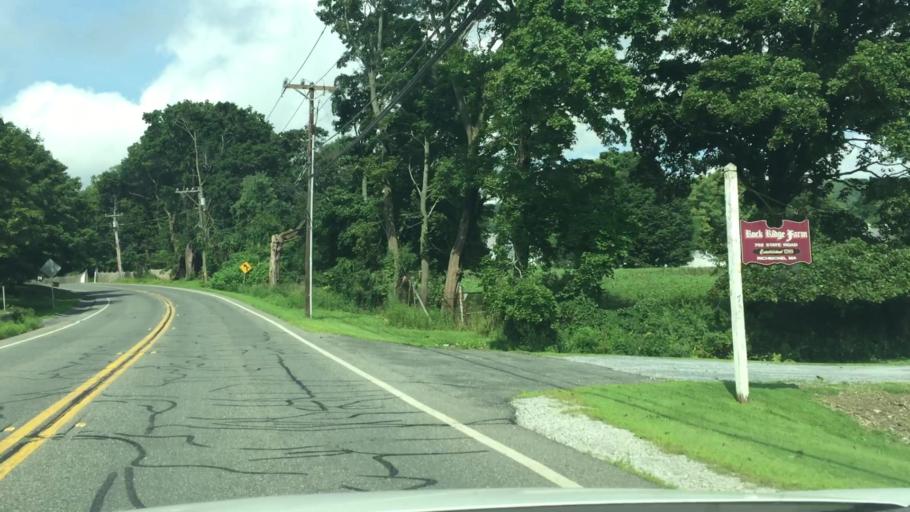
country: US
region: Massachusetts
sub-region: Berkshire County
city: Richmond
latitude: 42.4069
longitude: -73.3554
